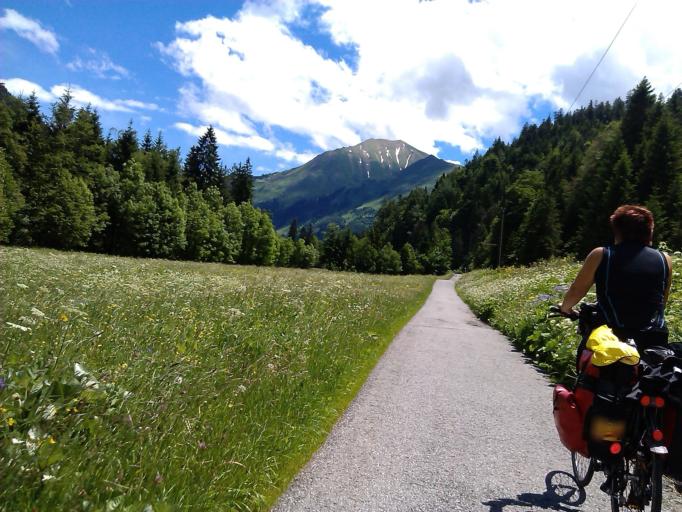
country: AT
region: Tyrol
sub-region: Politischer Bezirk Reutte
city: Bichlbach
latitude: 47.4317
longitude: 10.7678
